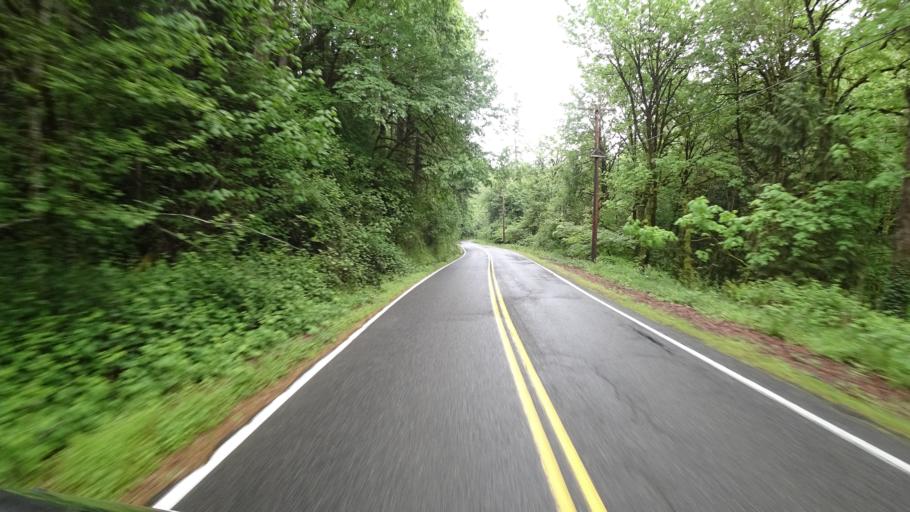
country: US
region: Oregon
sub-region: Washington County
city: West Haven-Sylvan
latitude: 45.5405
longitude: -122.7429
